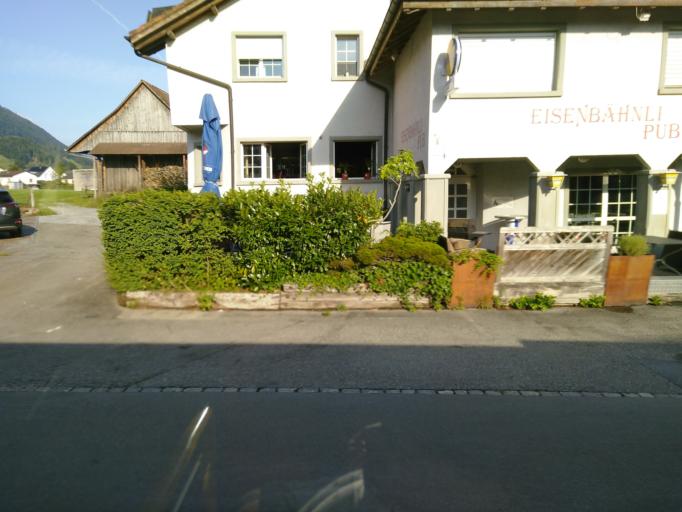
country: CH
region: Schwyz
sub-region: Bezirk March
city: Reichenburg
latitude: 47.1716
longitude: 8.9847
